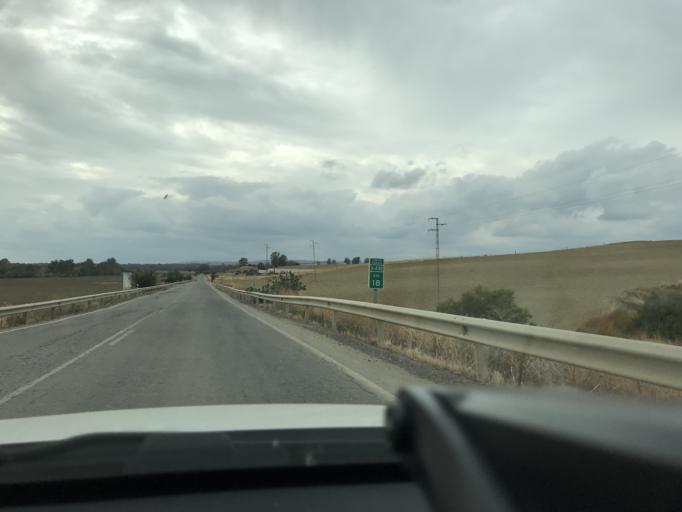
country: ES
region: Andalusia
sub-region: Provincia de Sevilla
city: Villanueva del Rio y Minas
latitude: 37.6355
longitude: -5.7113
